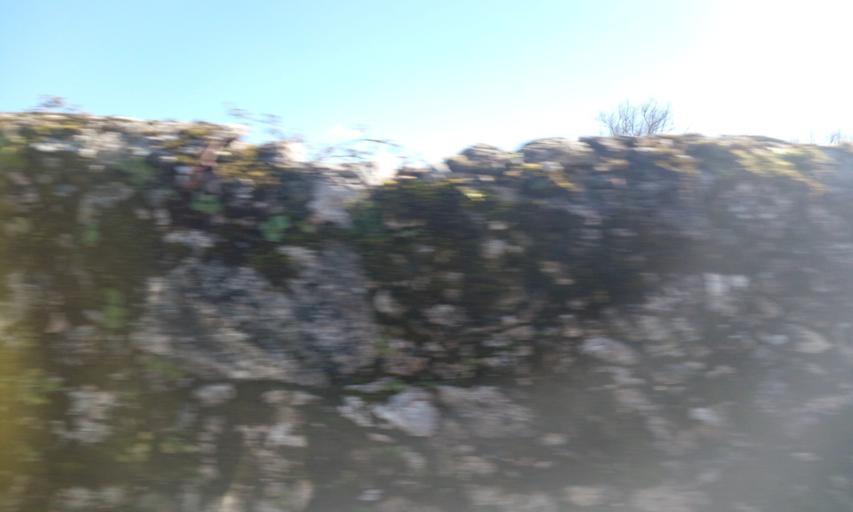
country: PT
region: Guarda
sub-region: Manteigas
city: Manteigas
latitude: 40.4887
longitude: -7.6054
